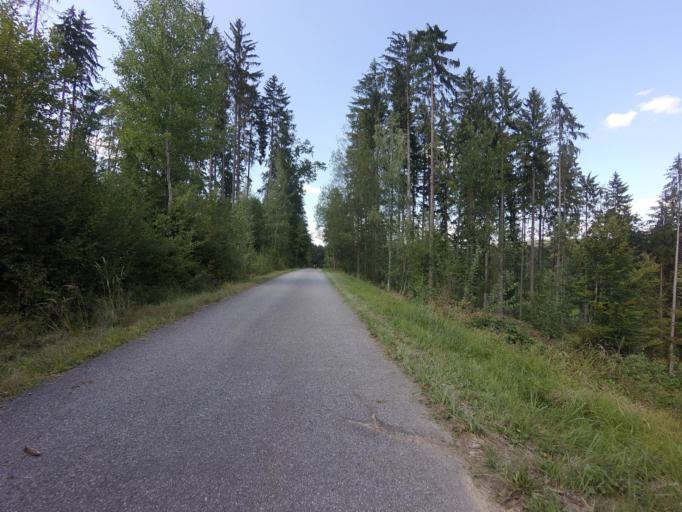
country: CZ
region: Jihocesky
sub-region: Okres Ceske Budejovice
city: Hluboka nad Vltavou
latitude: 49.1047
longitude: 14.4610
